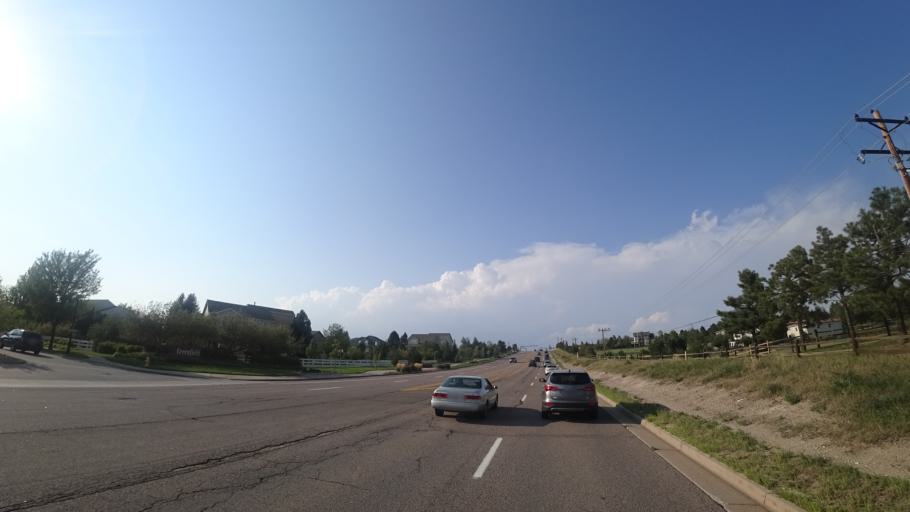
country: US
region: Colorado
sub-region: Douglas County
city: Parker
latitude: 39.6038
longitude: -104.7447
